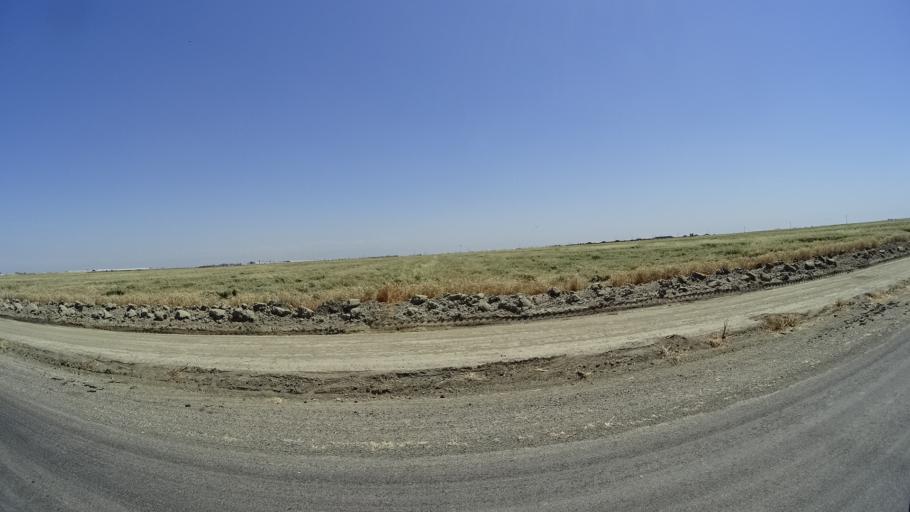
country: US
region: California
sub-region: Kings County
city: Stratford
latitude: 36.1935
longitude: -119.7086
